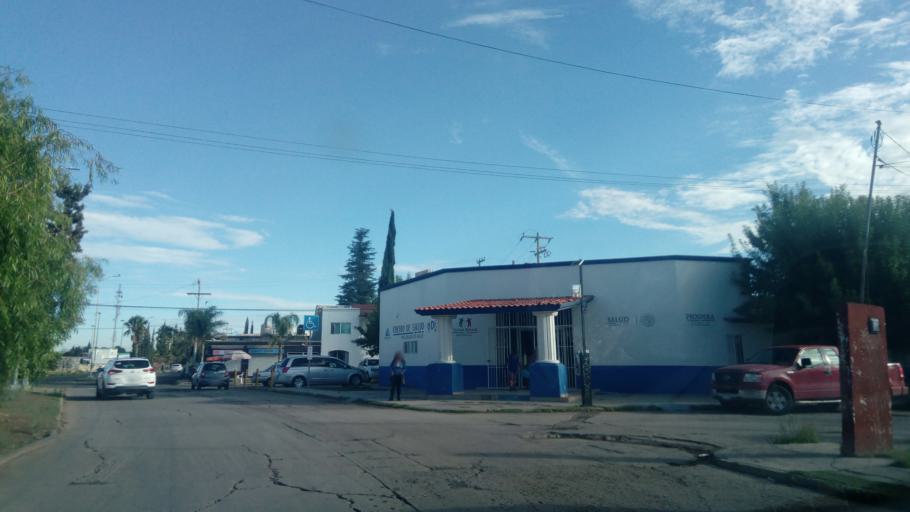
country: MX
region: Durango
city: Victoria de Durango
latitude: 24.0551
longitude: -104.6093
